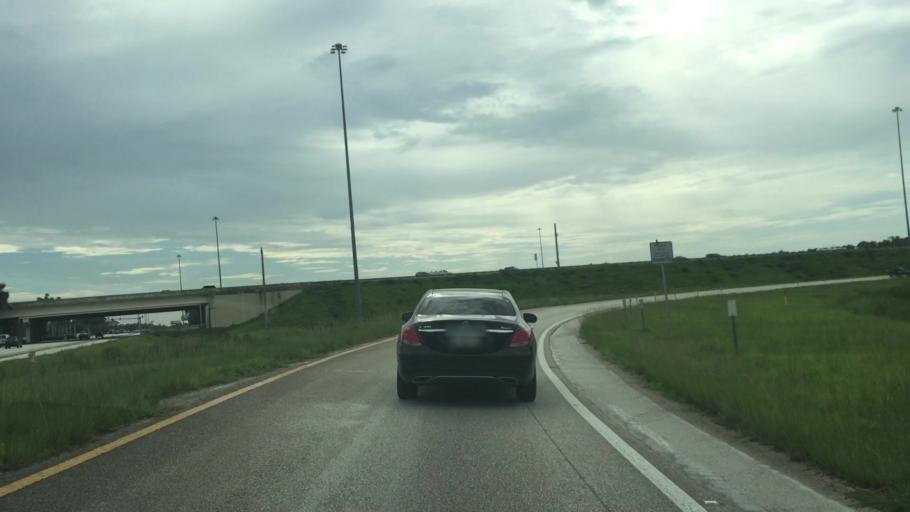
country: US
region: Florida
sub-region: Lee County
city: Three Oaks
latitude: 26.4934
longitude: -81.7921
